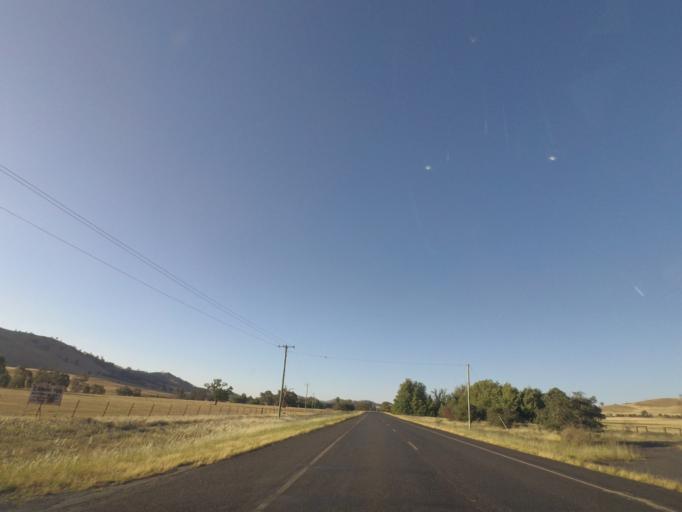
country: AU
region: New South Wales
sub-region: Gundagai
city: Gundagai
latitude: -34.9392
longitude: 148.1678
